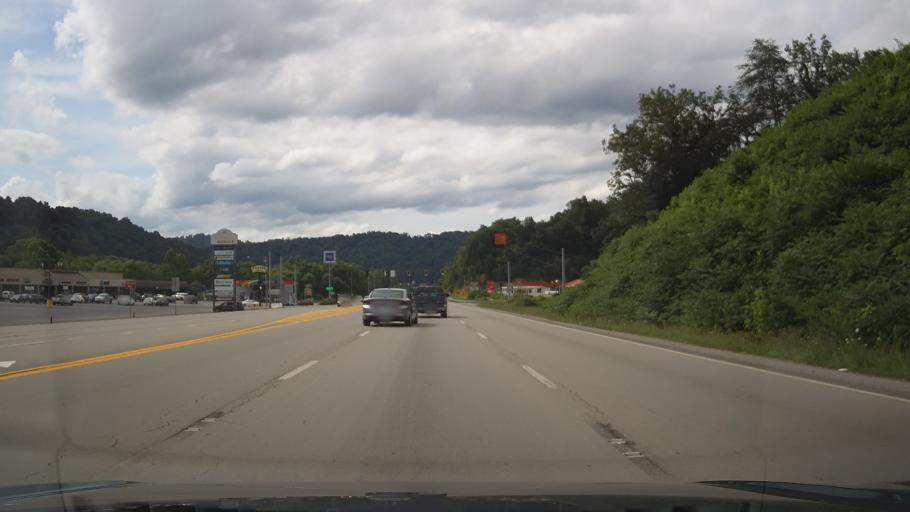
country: US
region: Kentucky
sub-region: Pike County
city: Coal Run Village
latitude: 37.5269
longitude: -82.5741
